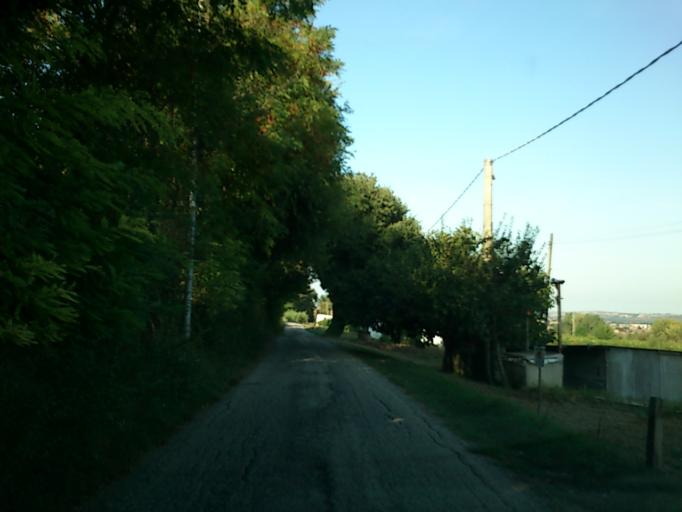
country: IT
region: The Marches
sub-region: Provincia di Pesaro e Urbino
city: Calcinelli
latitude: 43.7667
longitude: 12.9202
